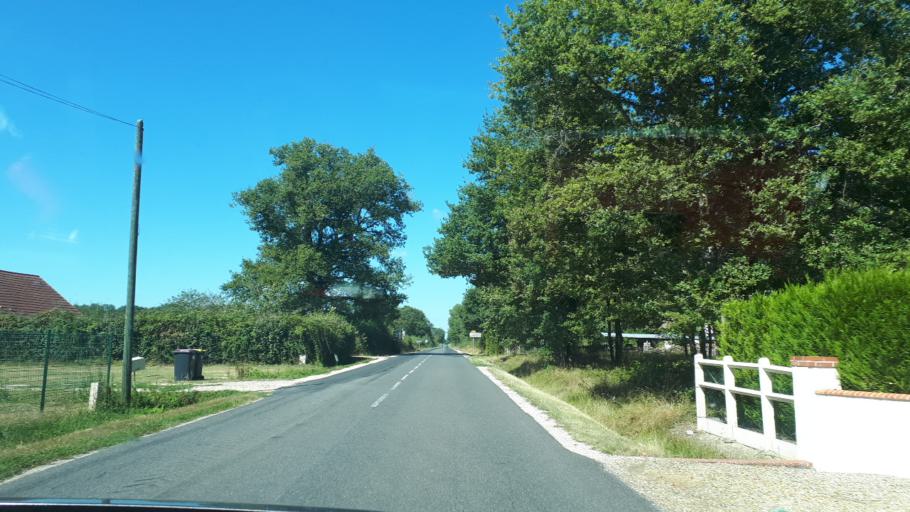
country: FR
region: Centre
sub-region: Departement du Loir-et-Cher
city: Vouzon
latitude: 47.6429
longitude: 2.1570
